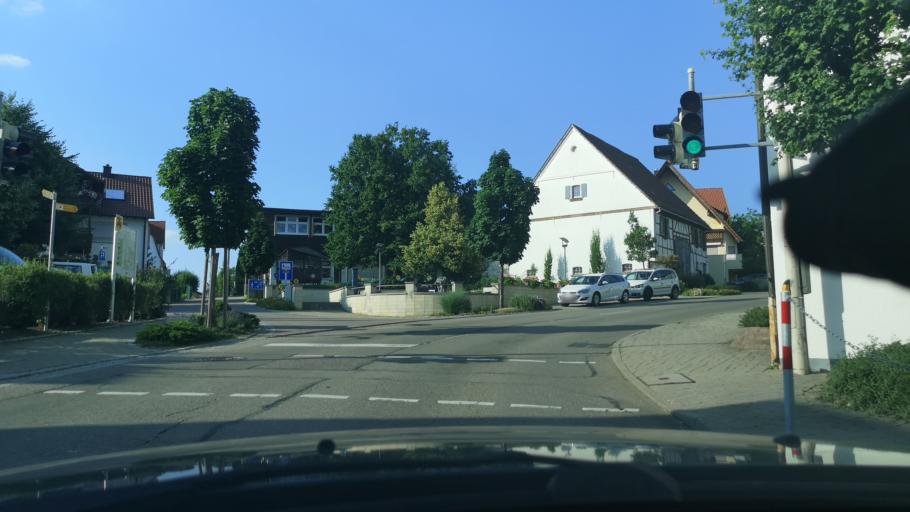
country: DE
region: Baden-Wuerttemberg
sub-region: Regierungsbezirk Stuttgart
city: Schlat
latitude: 48.6527
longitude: 9.7052
